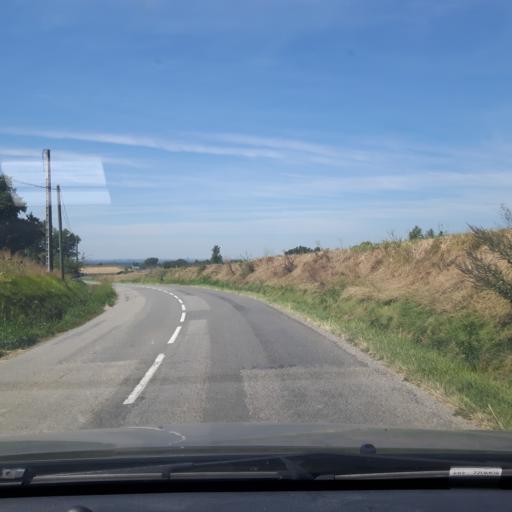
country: FR
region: Midi-Pyrenees
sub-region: Departement de la Haute-Garonne
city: Bouloc
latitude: 43.7696
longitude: 1.3953
